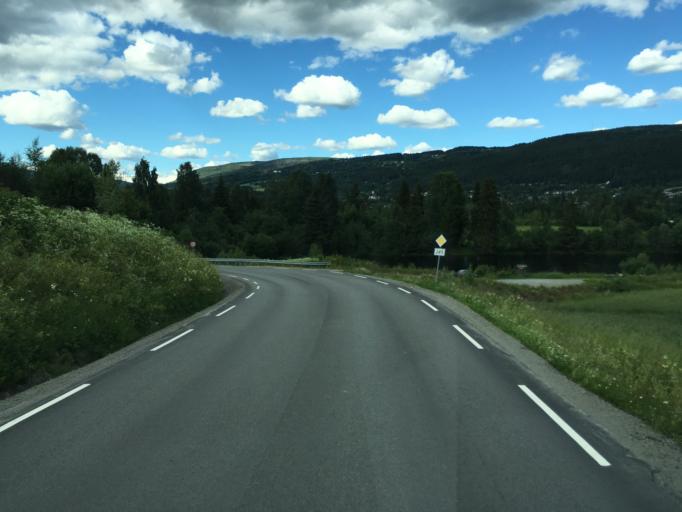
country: NO
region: Oppland
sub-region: Nordre Land
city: Dokka
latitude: 60.8225
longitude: 10.0736
